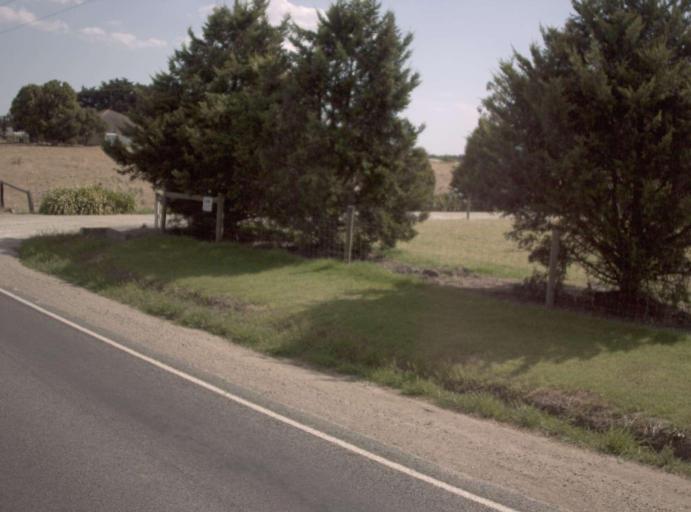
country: AU
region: Victoria
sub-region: Casey
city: Junction Village
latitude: -38.1360
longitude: 145.3238
